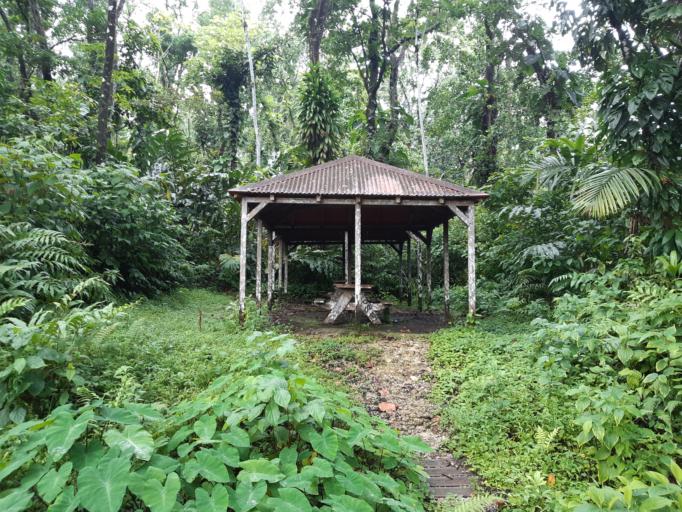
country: GP
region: Guadeloupe
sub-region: Guadeloupe
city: Capesterre-Belle-Eau
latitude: 16.0448
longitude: -61.6163
